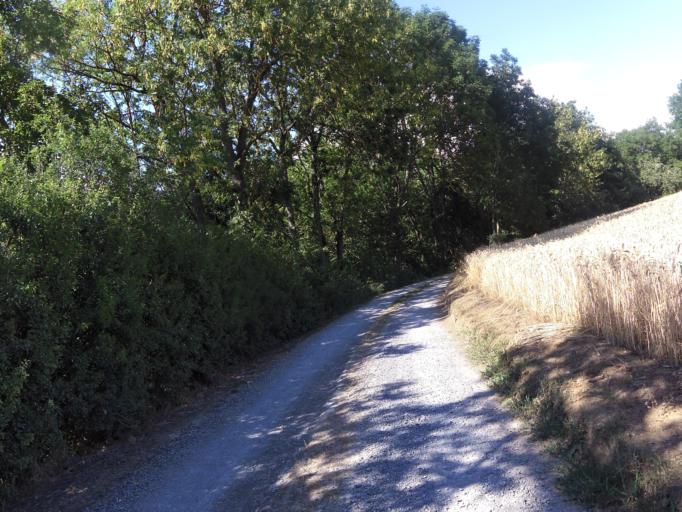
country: DE
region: Bavaria
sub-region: Regierungsbezirk Unterfranken
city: Rimpar
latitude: 49.8305
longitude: 9.9596
